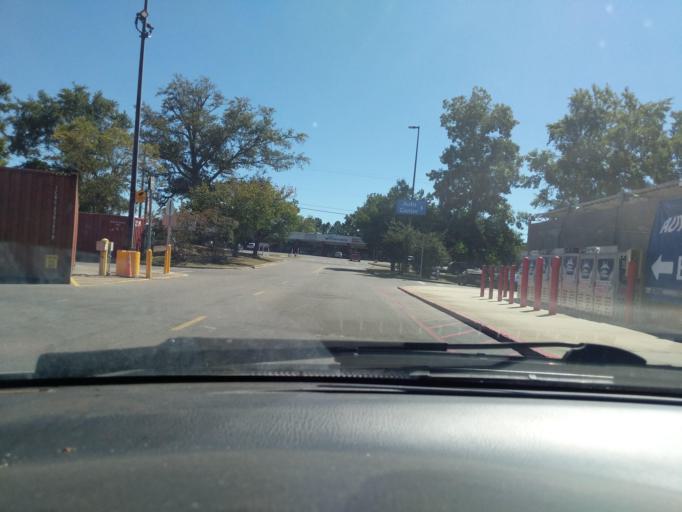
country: US
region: Alabama
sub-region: Houston County
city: Dothan
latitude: 31.1781
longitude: -85.4038
